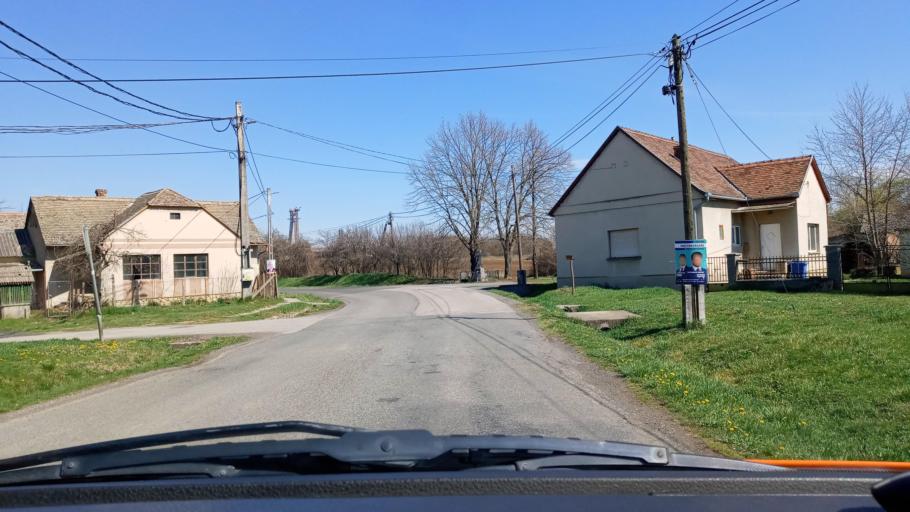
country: HU
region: Baranya
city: Boly
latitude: 46.0306
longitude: 18.4596
